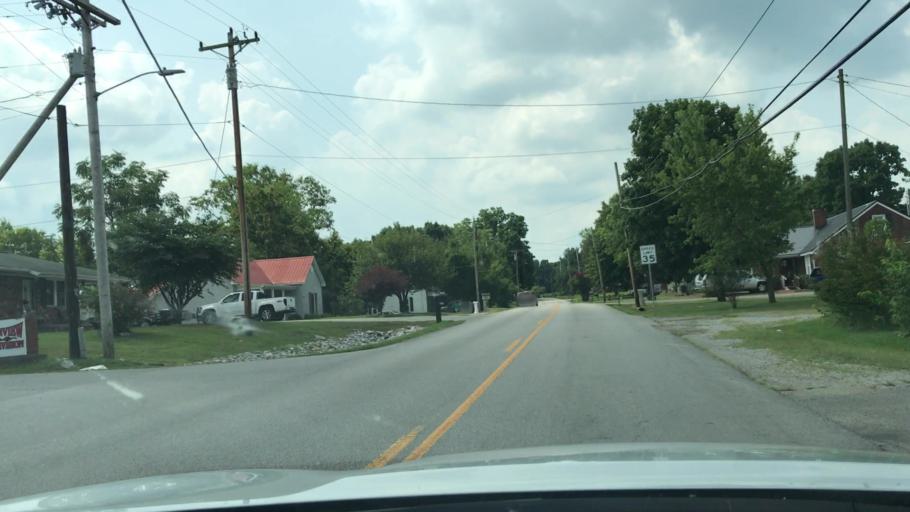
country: US
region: Kentucky
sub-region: Todd County
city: Elkton
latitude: 36.8037
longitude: -87.1486
